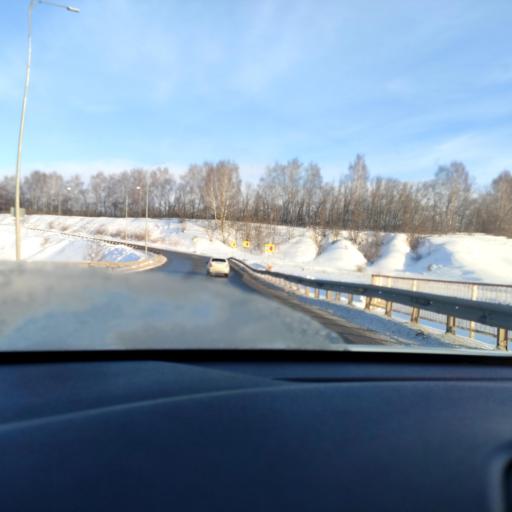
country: RU
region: Tatarstan
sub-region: Arskiy Rayon
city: Arsk
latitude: 56.1435
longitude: 49.9211
